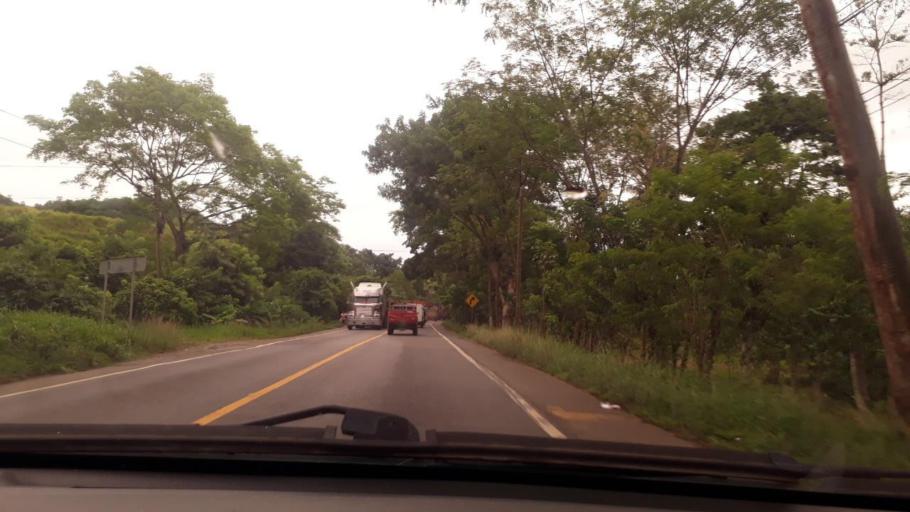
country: GT
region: Izabal
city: Morales
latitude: 15.5373
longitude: -88.7560
